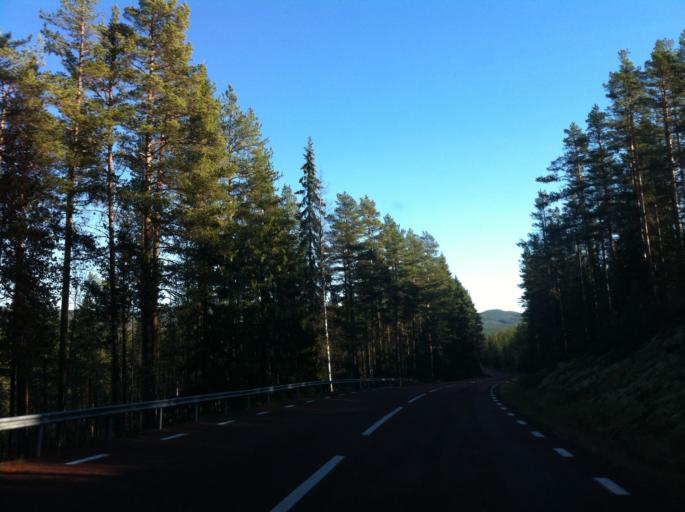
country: SE
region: Dalarna
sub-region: Alvdalens Kommun
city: AElvdalen
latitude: 61.3150
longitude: 13.6677
